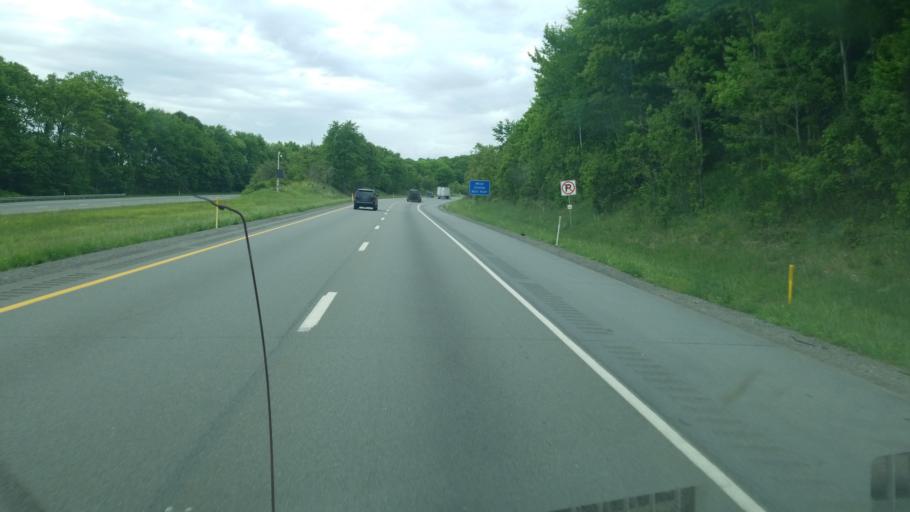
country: US
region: Pennsylvania
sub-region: Clarion County
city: Knox
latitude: 41.1915
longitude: -79.5121
